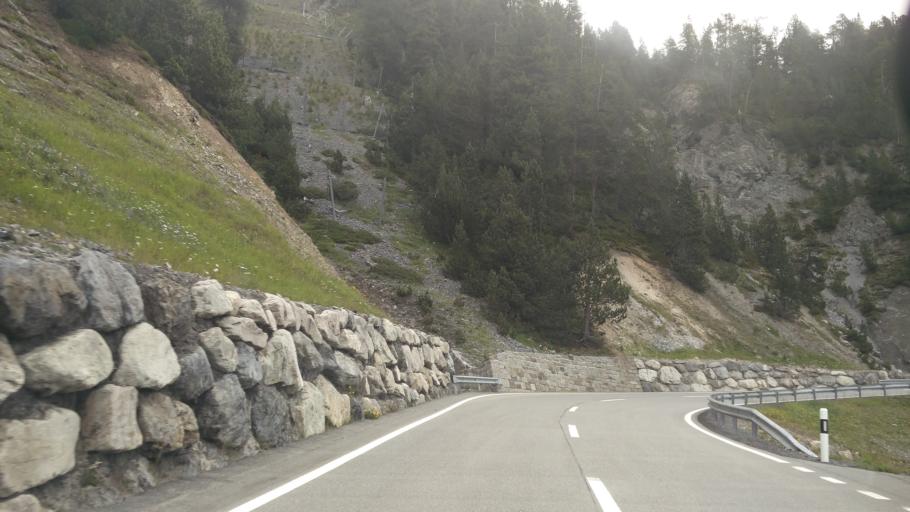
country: CH
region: Grisons
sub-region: Inn District
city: Scuol
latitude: 46.6436
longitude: 10.2851
